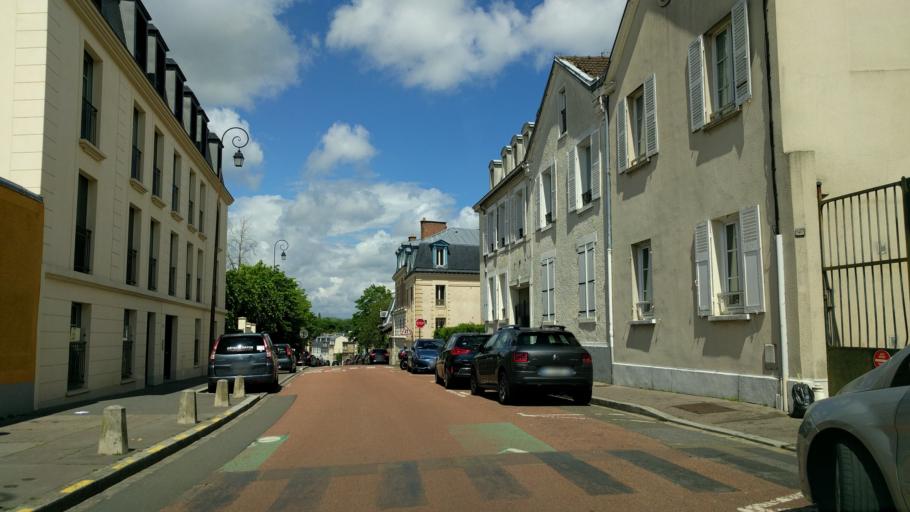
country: FR
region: Ile-de-France
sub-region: Departement des Yvelines
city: Le Chesnay
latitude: 48.8148
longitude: 2.1232
